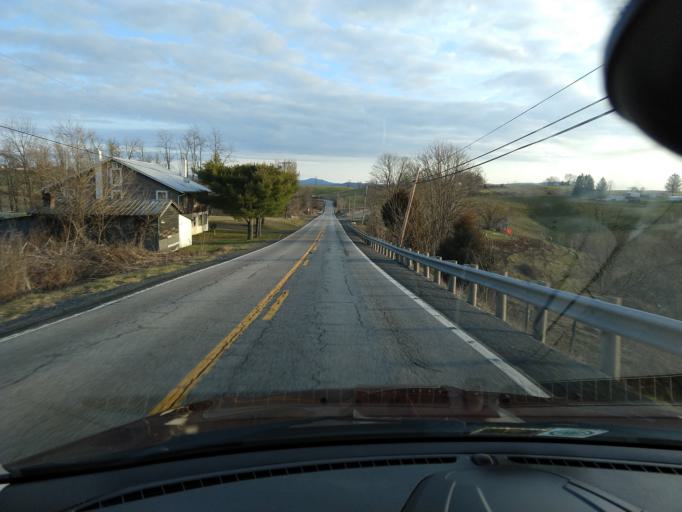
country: US
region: West Virginia
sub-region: Greenbrier County
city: Lewisburg
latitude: 37.9440
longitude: -80.3770
